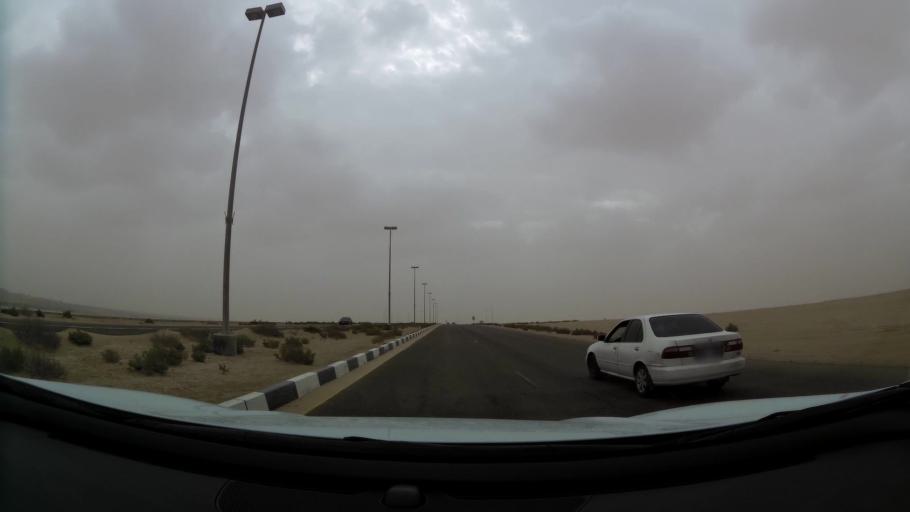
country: AE
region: Abu Dhabi
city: Abu Dhabi
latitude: 24.4628
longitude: 54.6860
